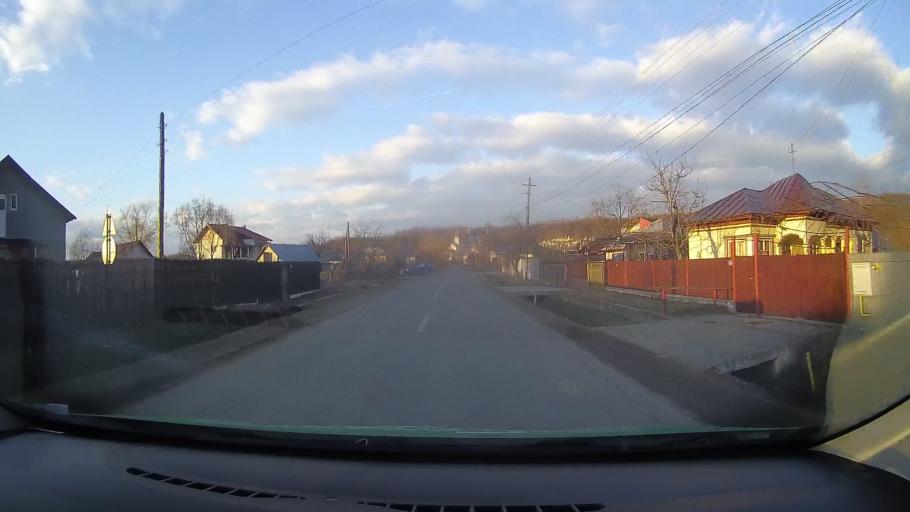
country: RO
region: Dambovita
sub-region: Comuna Gura Ocnitei
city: Adanca
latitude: 44.9164
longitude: 25.6159
